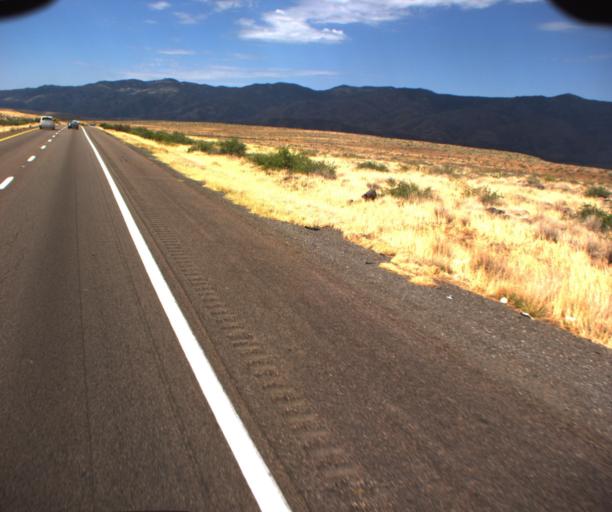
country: US
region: Arizona
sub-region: Yavapai County
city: Cordes Lakes
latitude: 34.2069
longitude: -112.1206
